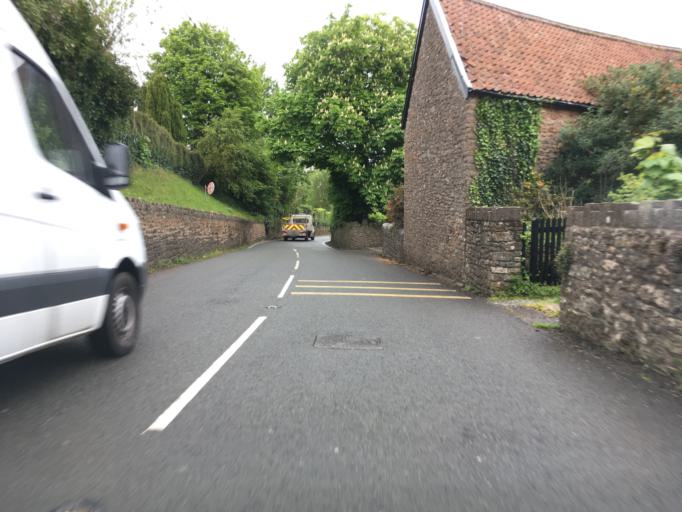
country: GB
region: England
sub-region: North Somerset
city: Blagdon
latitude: 51.3298
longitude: -2.7198
